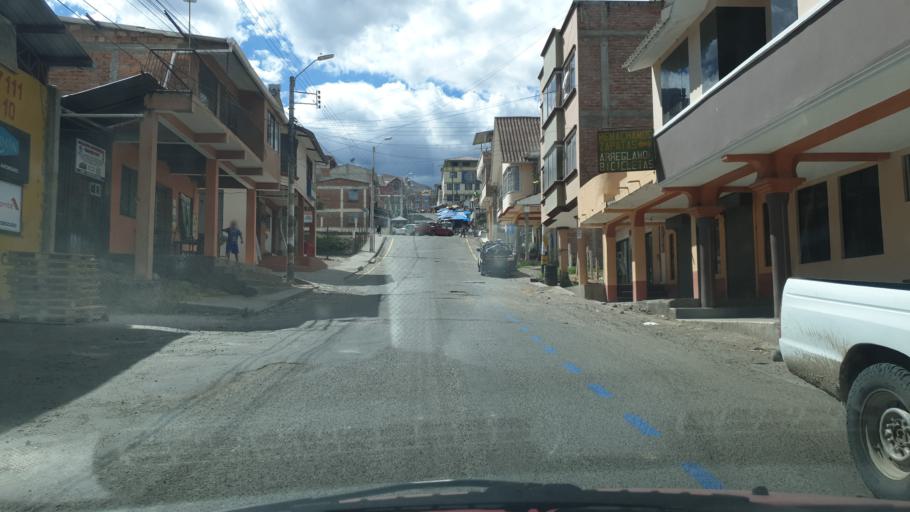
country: EC
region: Azuay
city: Cuenca
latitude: -3.2770
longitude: -79.3143
